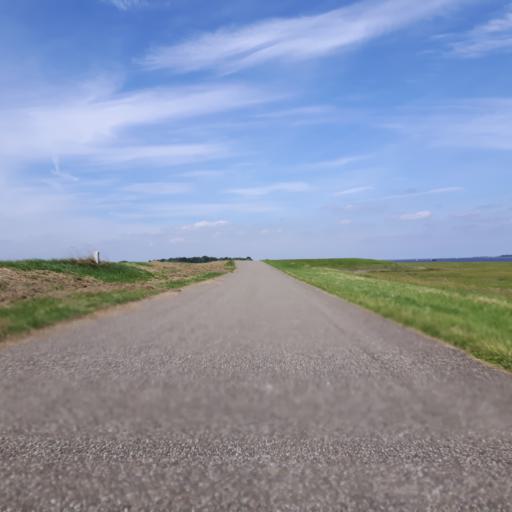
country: NL
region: Zeeland
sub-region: Schouwen-Duiveland
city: Bruinisse
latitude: 51.6465
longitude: 4.1558
